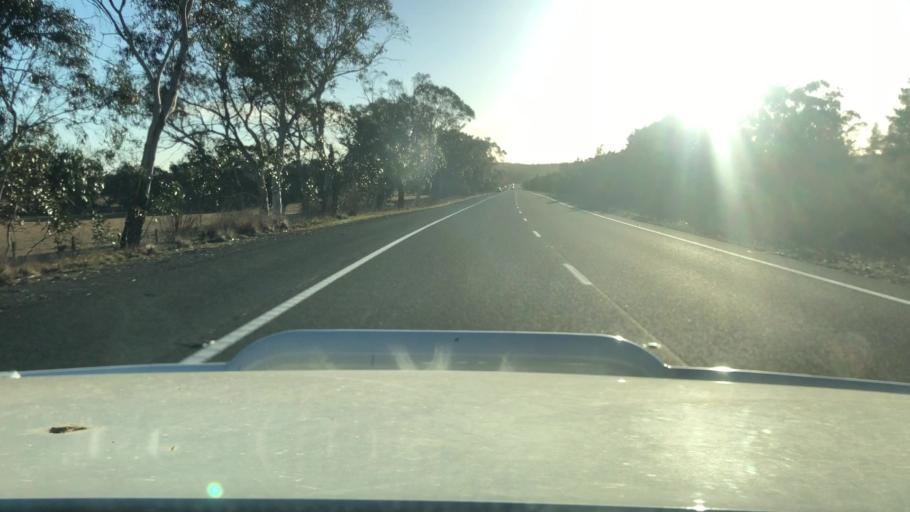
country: AU
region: New South Wales
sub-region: Wingecarribee
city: Bundanoon
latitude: -34.6626
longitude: 150.0741
